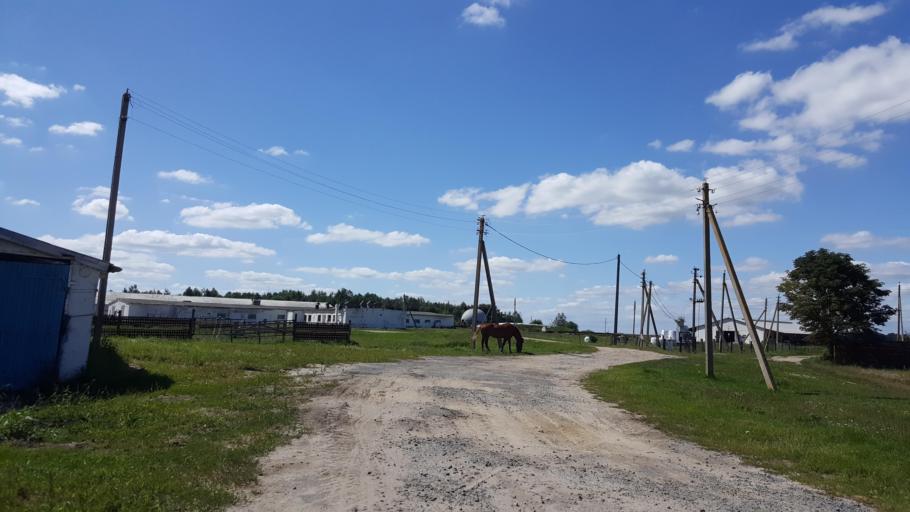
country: BY
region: Brest
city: Kobryn
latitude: 52.2960
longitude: 24.3332
